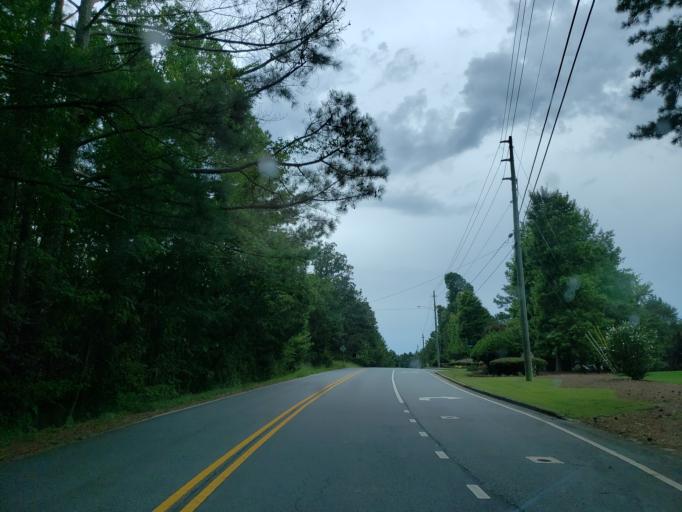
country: US
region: Georgia
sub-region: Cobb County
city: Acworth
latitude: 34.0204
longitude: -84.6970
